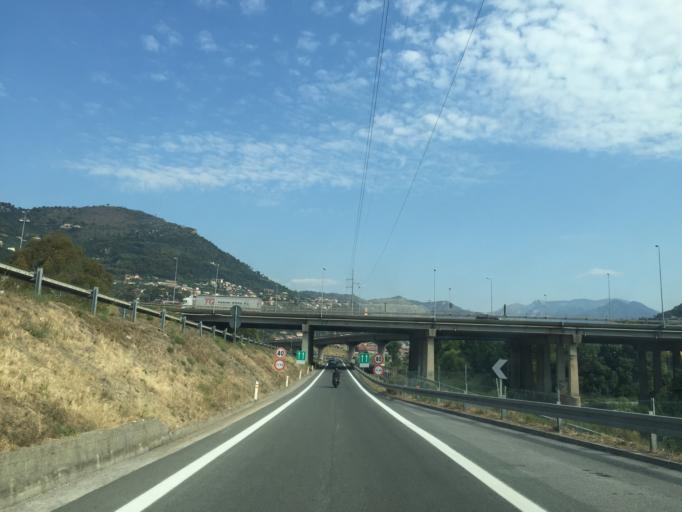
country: IT
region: Liguria
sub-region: Provincia di Imperia
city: Ventimiglia
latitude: 43.7997
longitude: 7.5965
